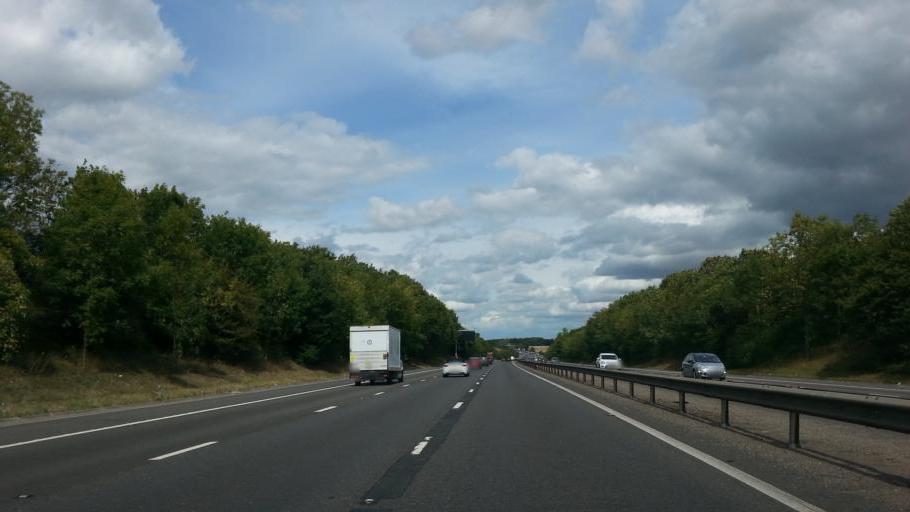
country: GB
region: England
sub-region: Hertfordshire
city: Sawbridgeworth
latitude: 51.7855
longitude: 0.1693
